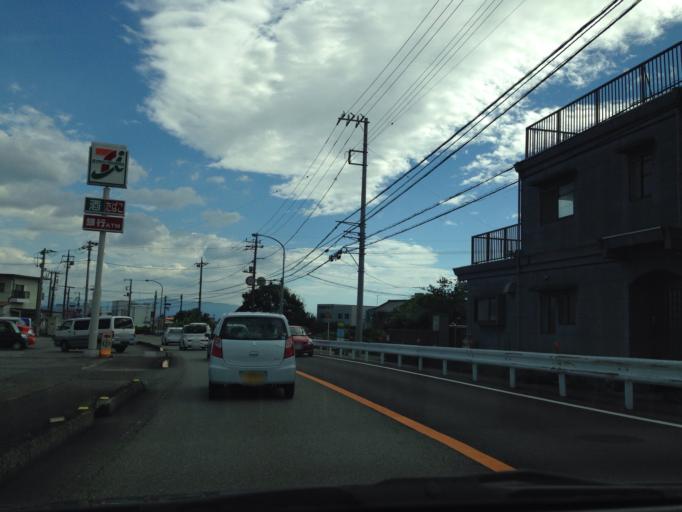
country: JP
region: Shizuoka
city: Mishima
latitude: 35.1965
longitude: 138.9138
